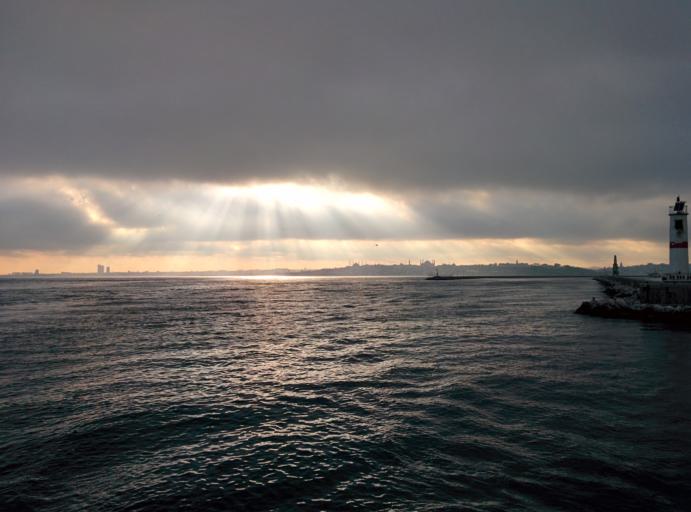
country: TR
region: Istanbul
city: UEskuedar
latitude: 40.9942
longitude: 29.0222
